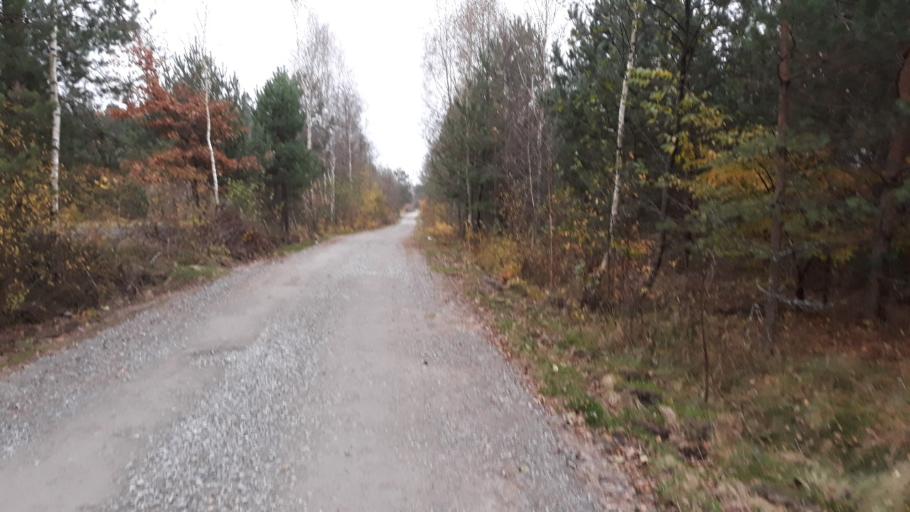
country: PL
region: Lublin Voivodeship
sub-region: Powiat janowski
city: Dzwola
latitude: 50.6492
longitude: 22.5727
